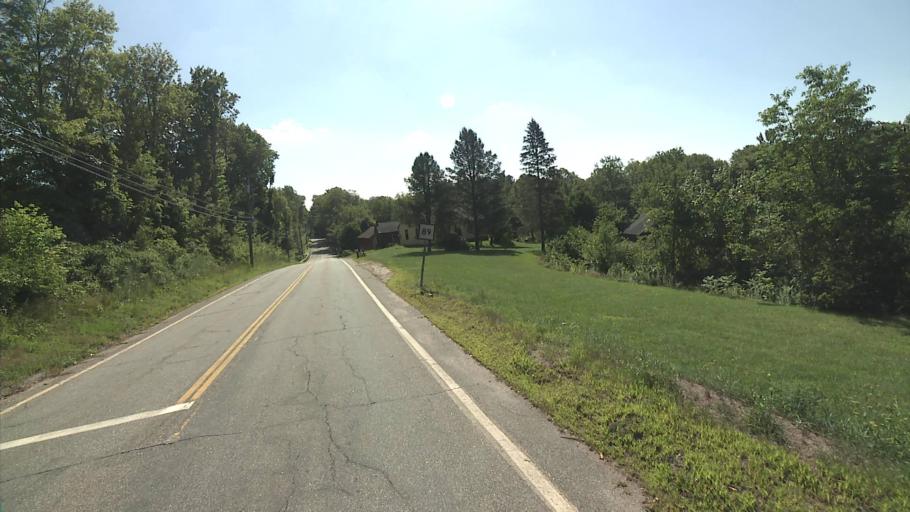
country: US
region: Connecticut
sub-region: Tolland County
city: Stafford Springs
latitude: 41.9173
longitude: -72.1916
